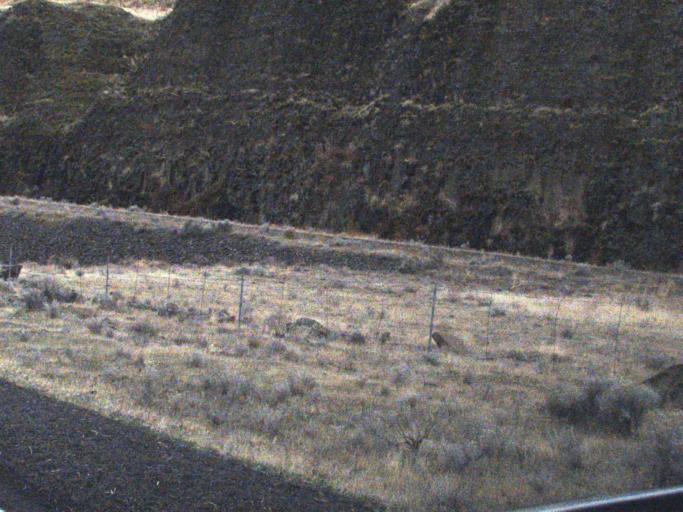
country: US
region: Washington
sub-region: Walla Walla County
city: Waitsburg
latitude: 46.5607
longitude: -118.1832
